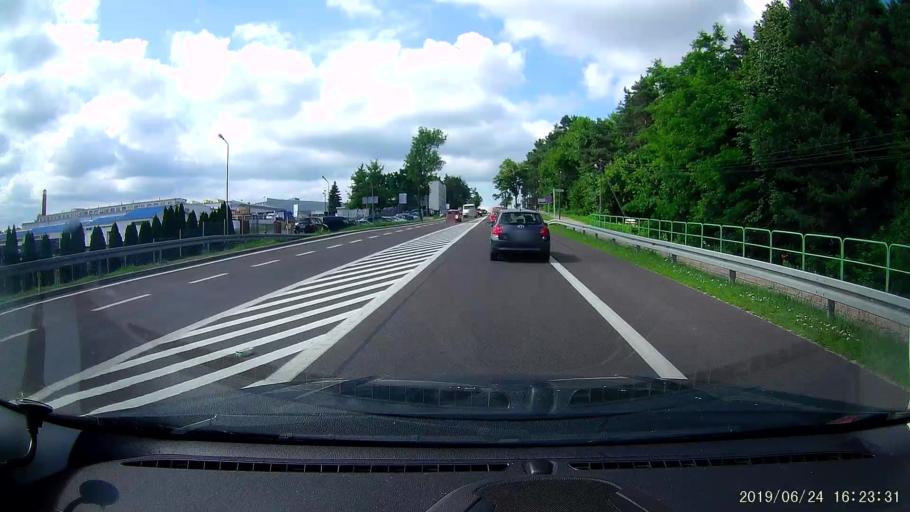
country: PL
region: Lublin Voivodeship
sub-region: Powiat tomaszowski
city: Tomaszow Lubelski
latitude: 50.4325
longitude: 23.4212
